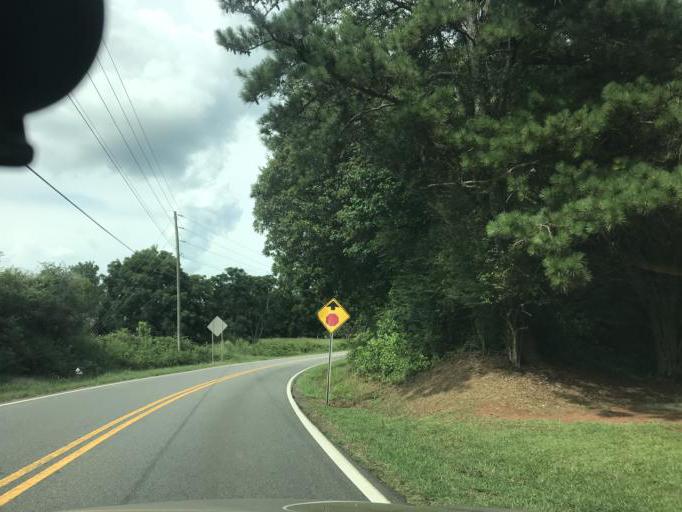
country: US
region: Georgia
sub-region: Forsyth County
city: Cumming
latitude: 34.2430
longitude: -84.2517
